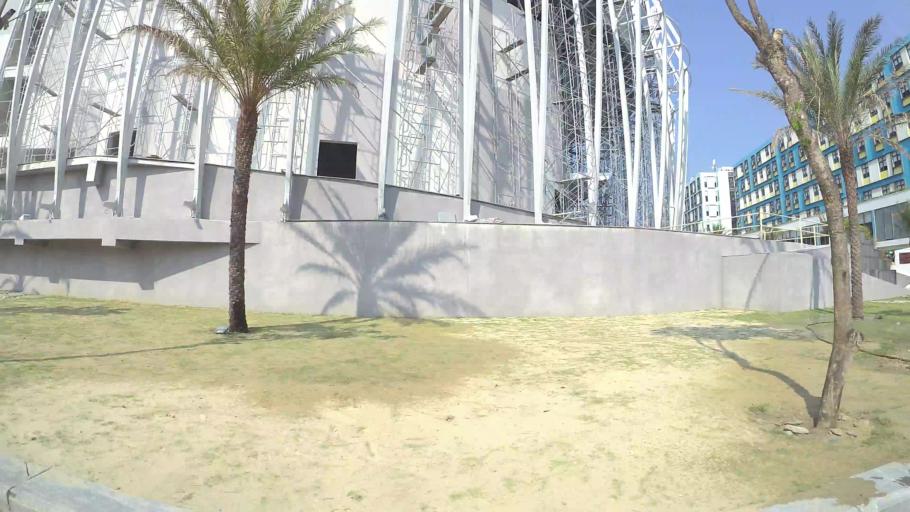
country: VN
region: Da Nang
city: Ngu Hanh Son
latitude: 15.9633
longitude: 108.2785
